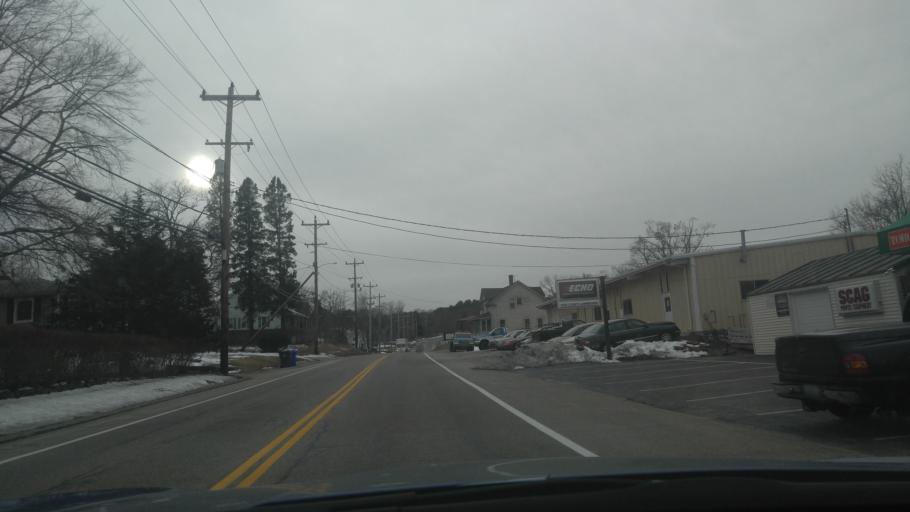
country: US
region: Rhode Island
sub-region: Kent County
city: West Warwick
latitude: 41.6800
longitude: -71.5318
